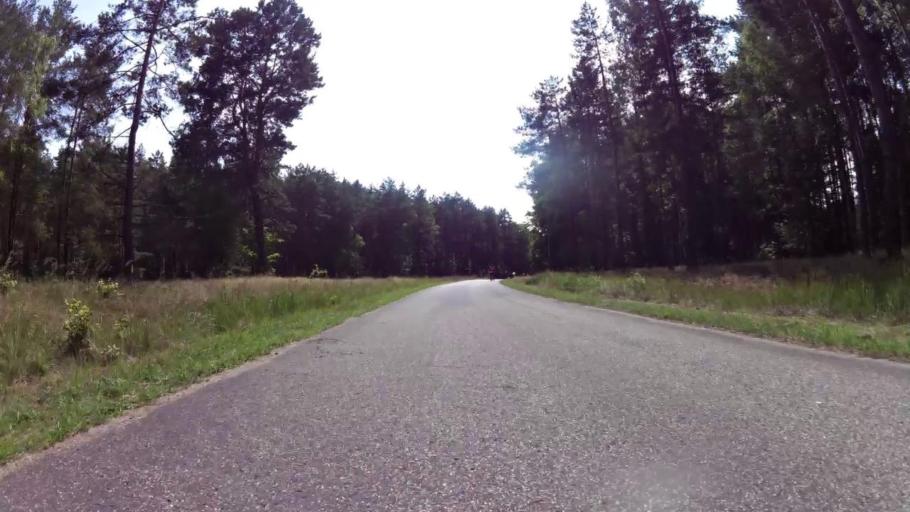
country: PL
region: West Pomeranian Voivodeship
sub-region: Powiat choszczenski
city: Drawno
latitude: 53.3700
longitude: 15.7234
